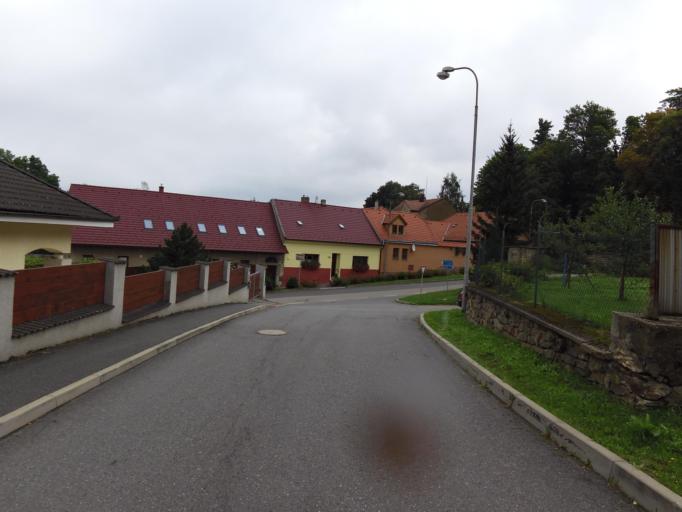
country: CZ
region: Jihocesky
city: Mlada Vozice
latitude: 49.5342
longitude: 14.8082
